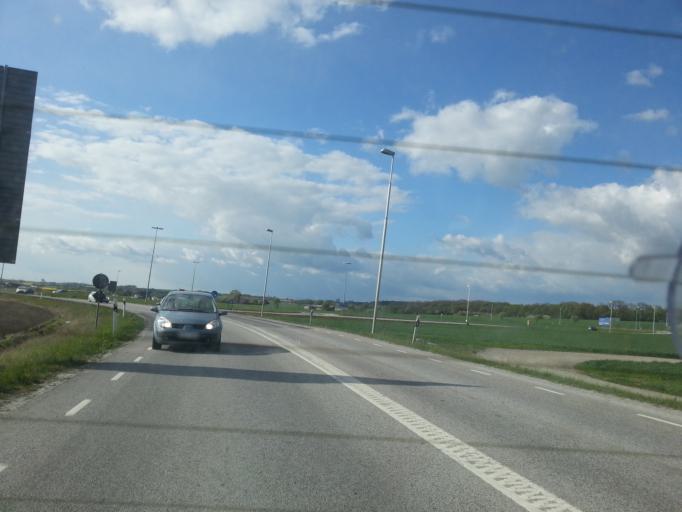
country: SE
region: Skane
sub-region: Lunds Kommun
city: Genarp
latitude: 55.6636
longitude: 13.3317
